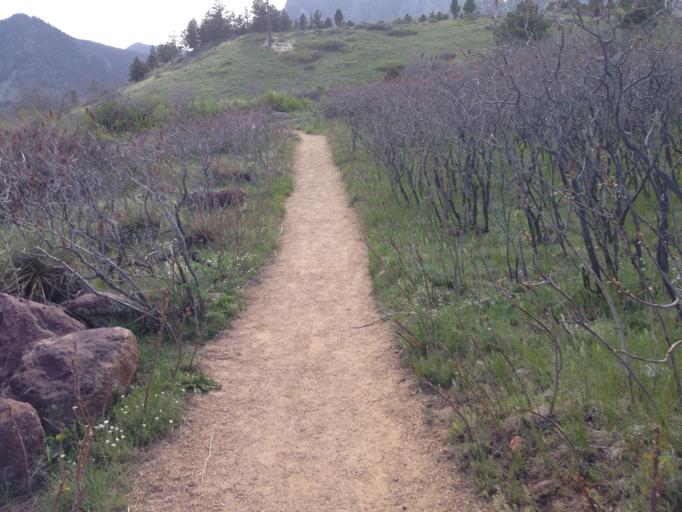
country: US
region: Colorado
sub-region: Boulder County
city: Boulder
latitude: 39.9415
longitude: -105.2614
